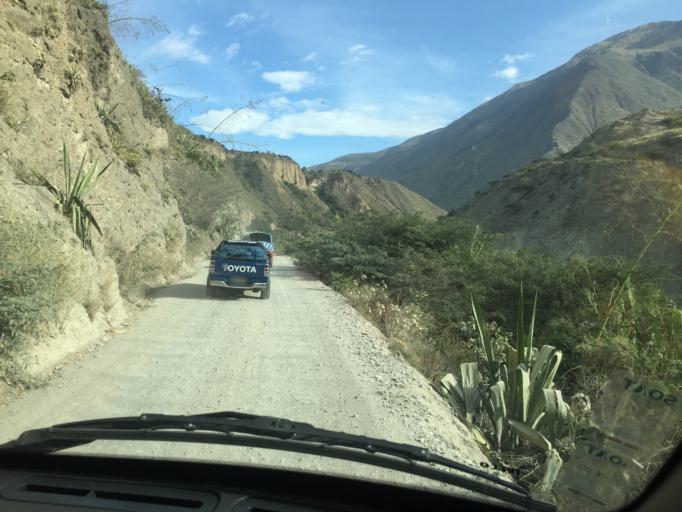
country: EC
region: Carchi
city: El Angel
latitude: 0.6000
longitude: -78.1379
